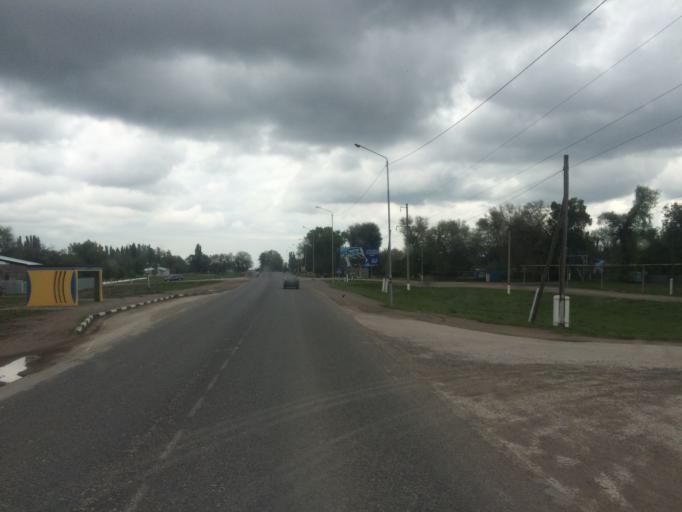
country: KZ
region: Zhambyl
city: Georgiyevka
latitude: 43.1428
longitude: 74.6164
